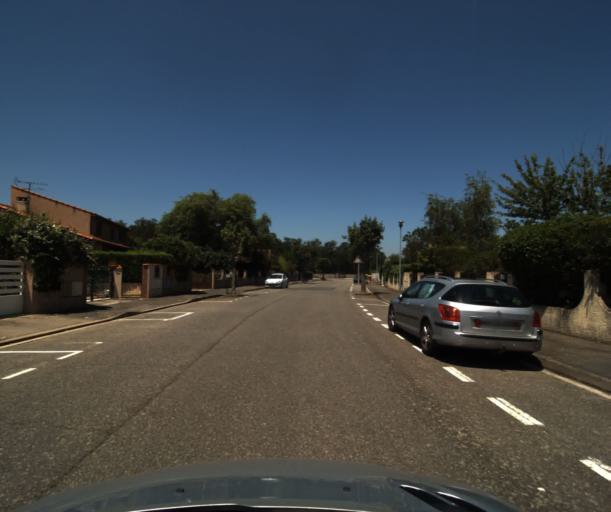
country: FR
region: Midi-Pyrenees
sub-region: Departement de la Haute-Garonne
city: Roquettes
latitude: 43.4926
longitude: 1.3728
